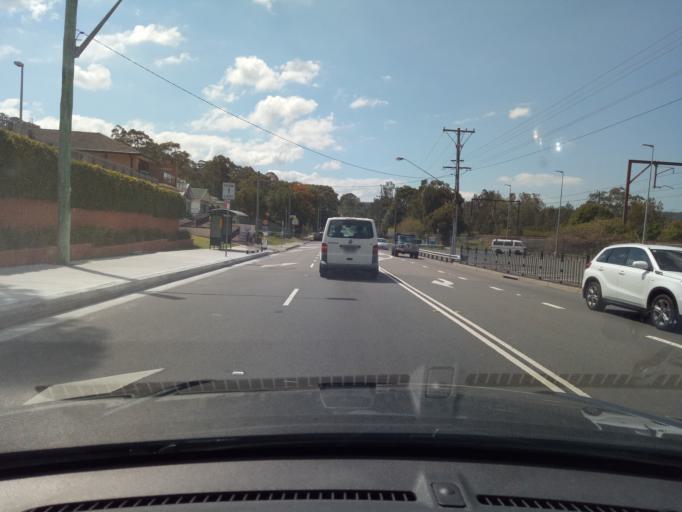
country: AU
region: New South Wales
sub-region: Gosford Shire
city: Point Clare
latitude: -33.4457
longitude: 151.3282
